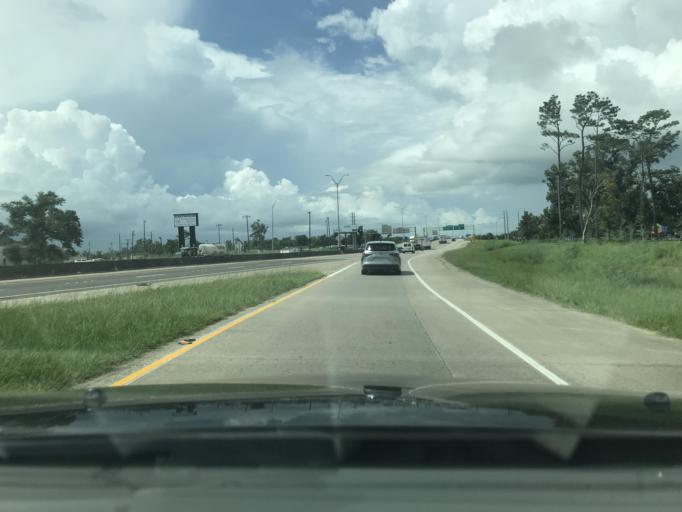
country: US
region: Louisiana
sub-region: Calcasieu Parish
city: Lake Charles
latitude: 30.2455
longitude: -93.1823
